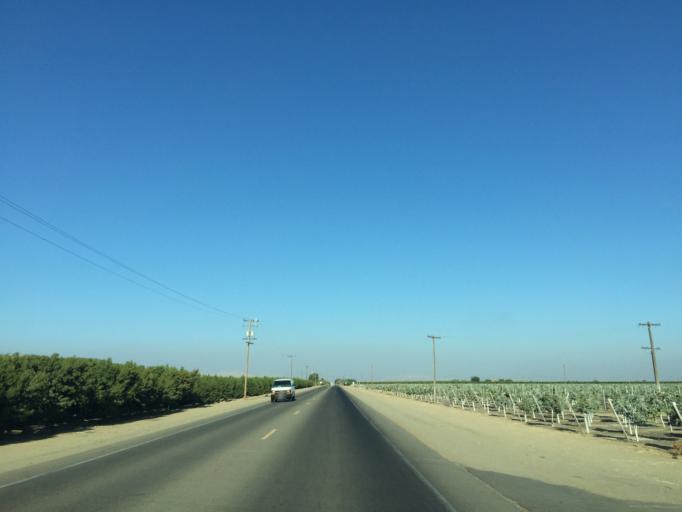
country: US
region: California
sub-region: Tulare County
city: London
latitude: 36.4883
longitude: -119.4444
